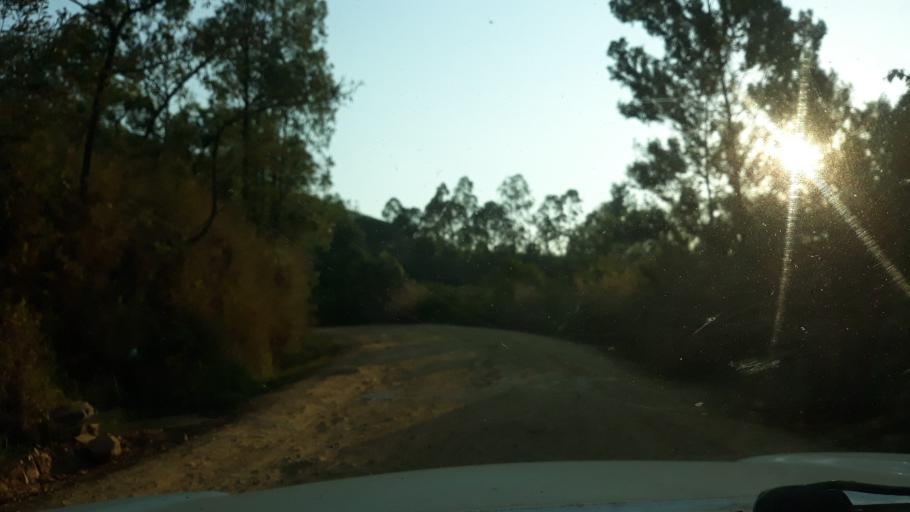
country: RW
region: Western Province
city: Cyangugu
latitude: -2.6988
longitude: 28.9065
